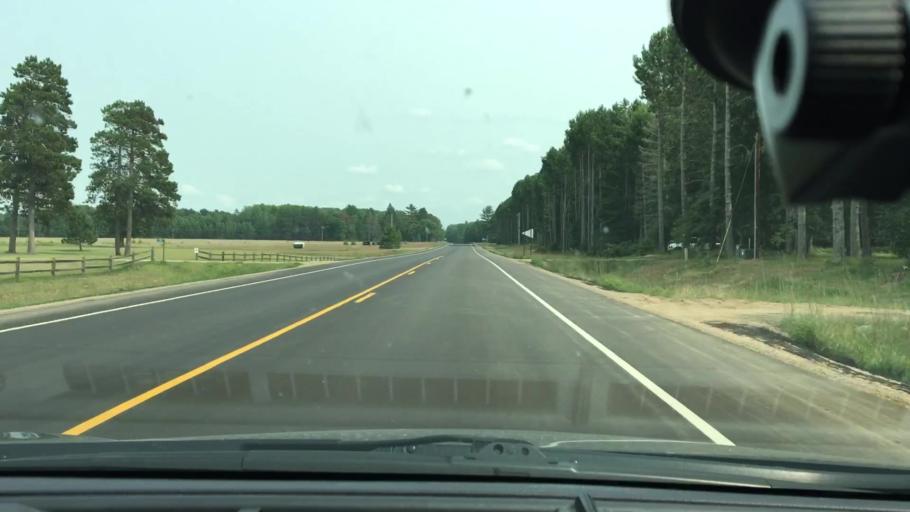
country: US
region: Minnesota
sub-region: Crow Wing County
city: Nisswa
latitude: 46.5293
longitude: -94.2529
